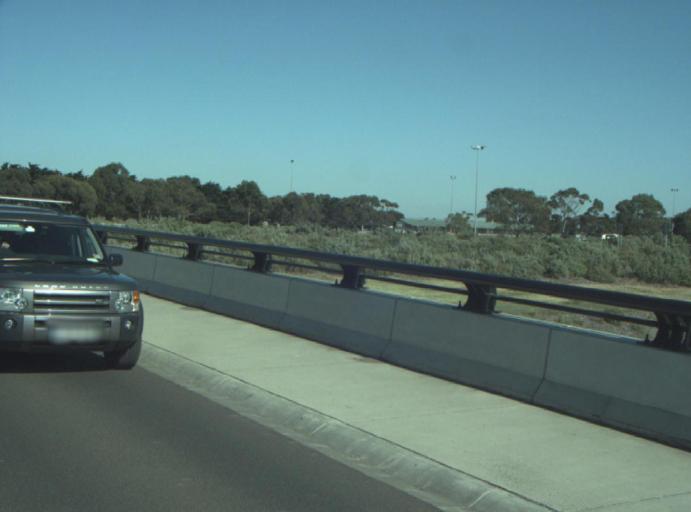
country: AU
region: Victoria
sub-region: Greater Geelong
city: Bell Post Hill
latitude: -38.0971
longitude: 144.3213
